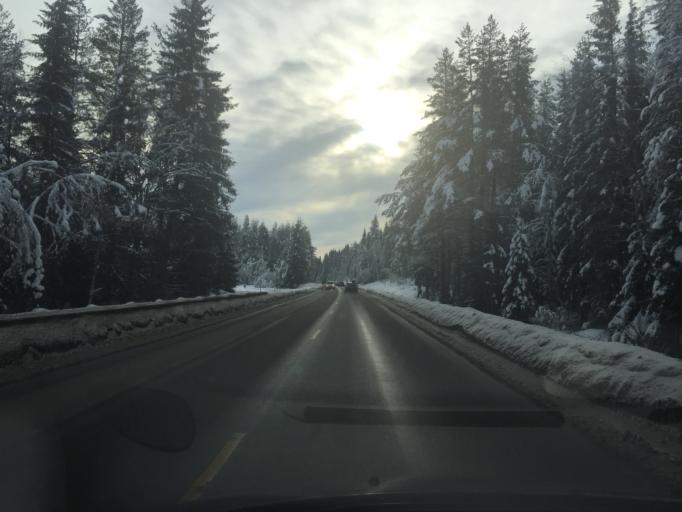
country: NO
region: Hedmark
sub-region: Trysil
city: Innbygda
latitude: 61.2814
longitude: 12.2836
